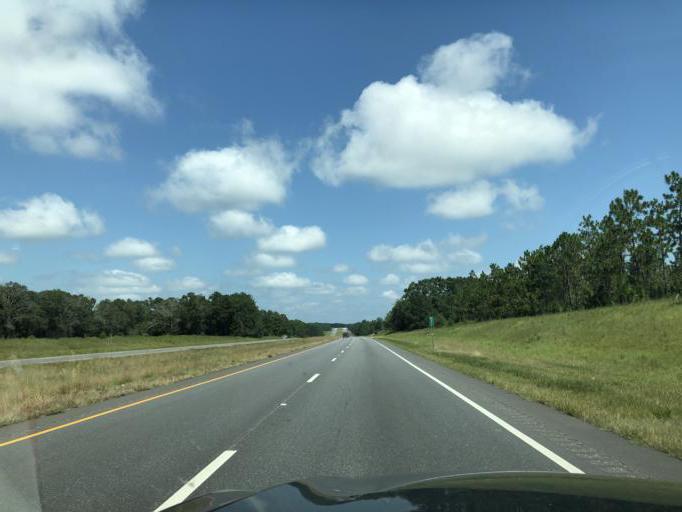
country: US
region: Alabama
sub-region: Henry County
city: Abbeville
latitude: 31.5120
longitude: -85.2908
